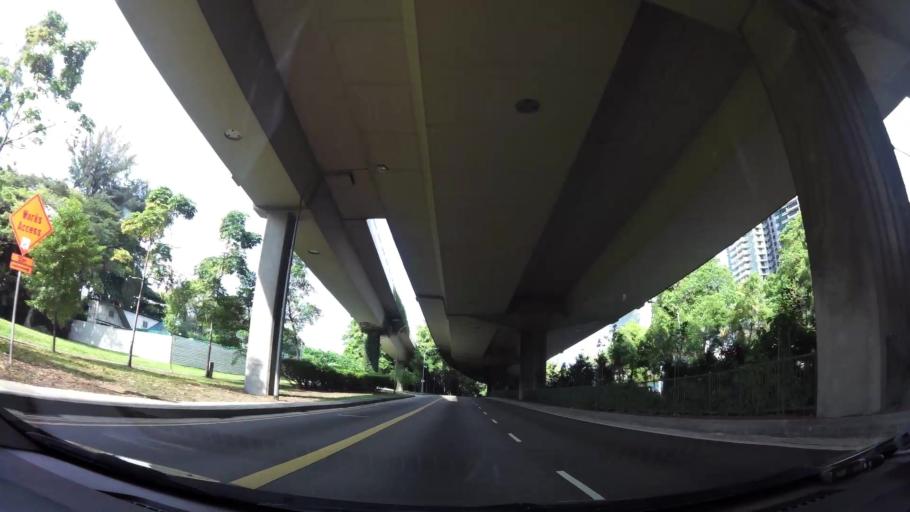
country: SG
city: Singapore
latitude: 1.2709
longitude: 103.8087
